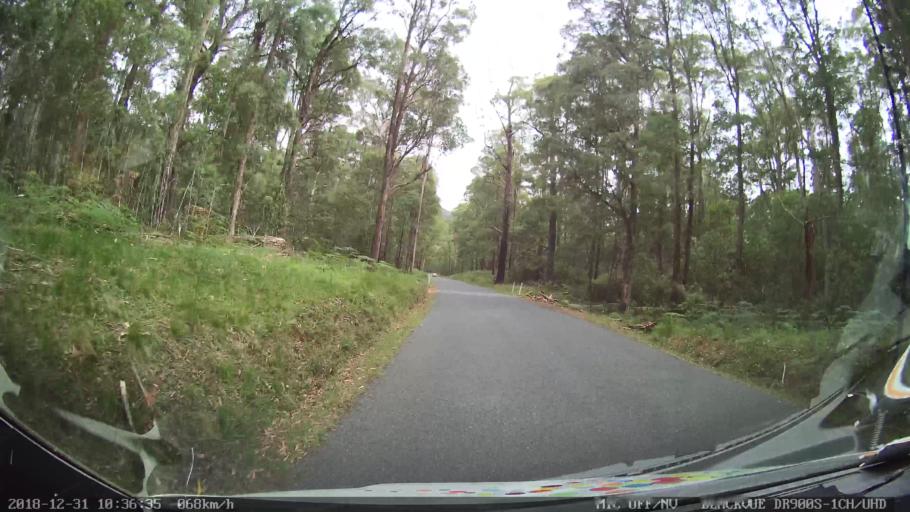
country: AU
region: New South Wales
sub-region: Snowy River
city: Jindabyne
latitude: -36.4247
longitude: 148.1715
